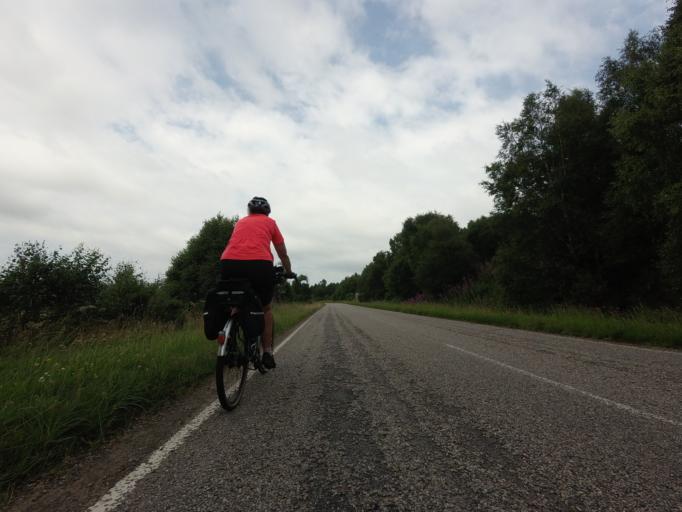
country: GB
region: Scotland
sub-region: Highland
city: Evanton
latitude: 57.9361
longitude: -4.4051
